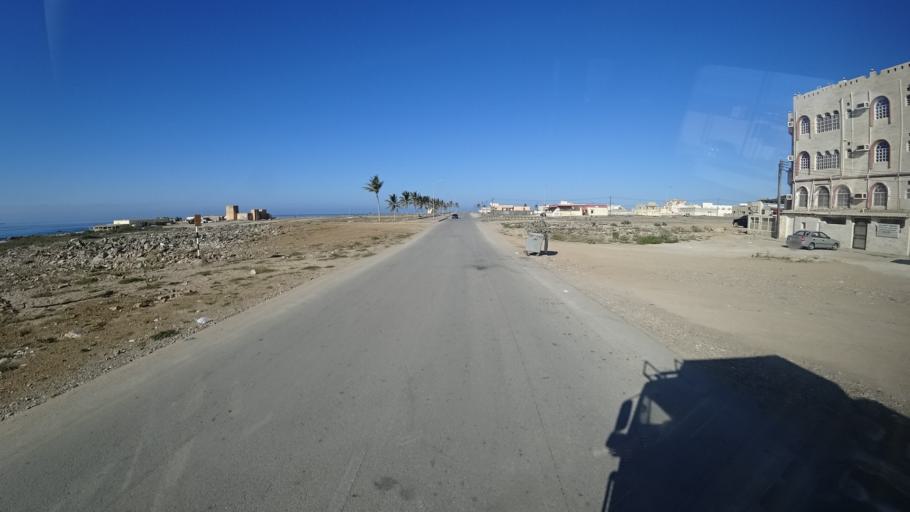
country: OM
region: Zufar
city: Salalah
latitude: 16.9778
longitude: 54.6944
